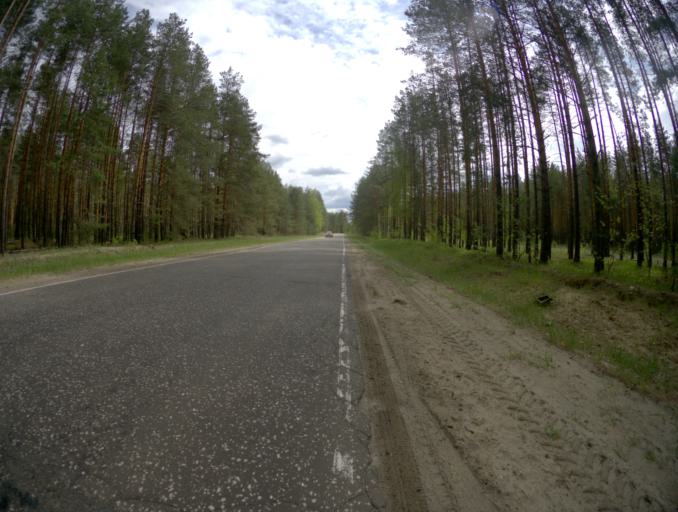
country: RU
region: Vladimir
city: Velikodvorskiy
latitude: 55.3970
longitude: 40.6924
